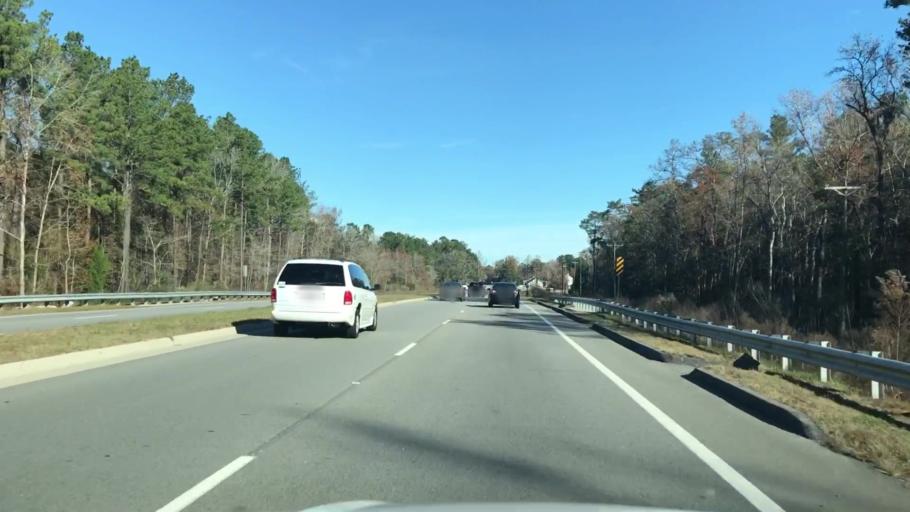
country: US
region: South Carolina
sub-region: Dorchester County
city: Centerville
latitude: 32.9546
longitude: -80.2015
